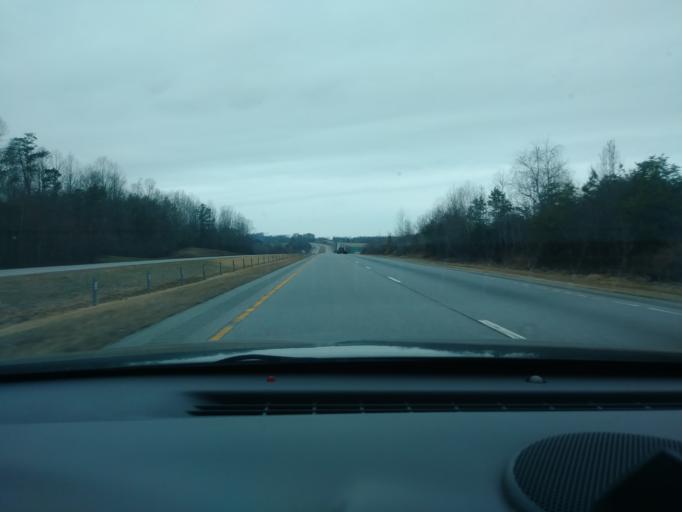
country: US
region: North Carolina
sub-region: Yadkin County
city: Jonesville
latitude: 36.1355
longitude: -80.8562
